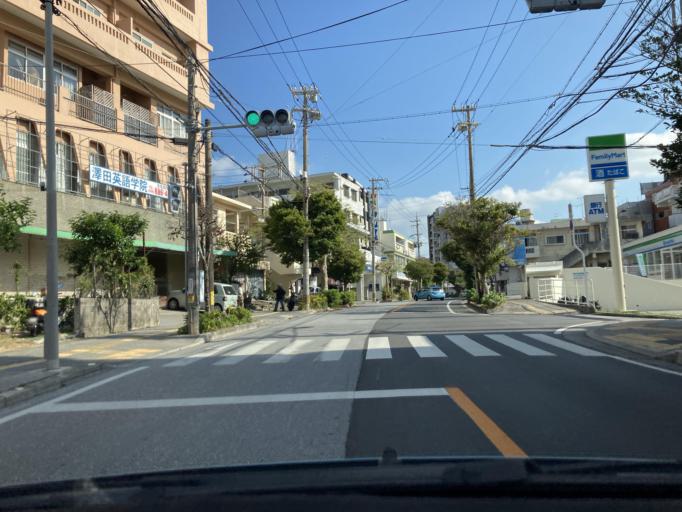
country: JP
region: Okinawa
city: Naha-shi
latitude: 26.2284
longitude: 127.7202
